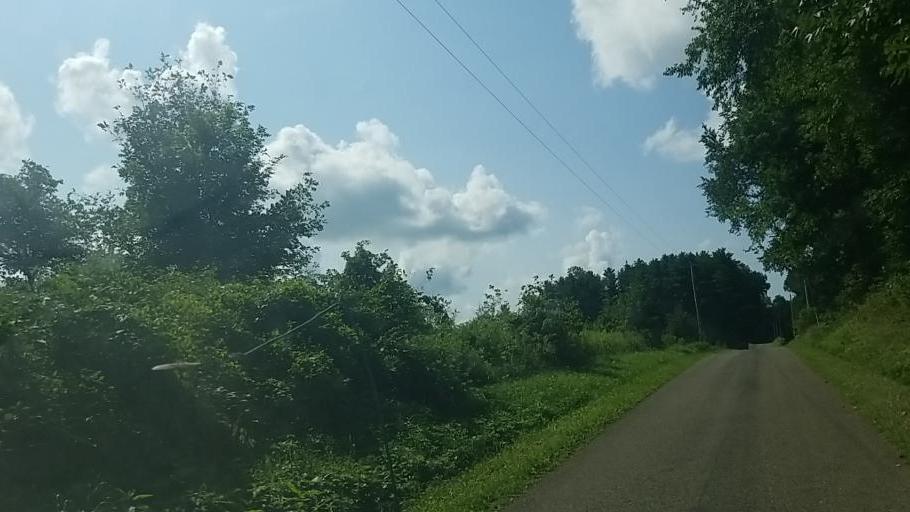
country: US
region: Ohio
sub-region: Ashland County
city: Ashland
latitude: 40.7446
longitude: -82.2980
